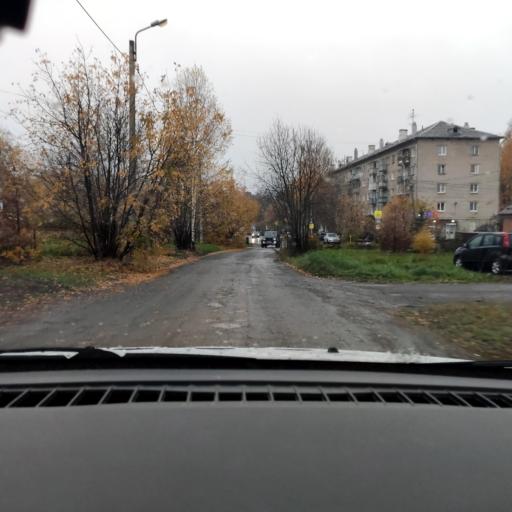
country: RU
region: Perm
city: Kondratovo
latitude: 58.0490
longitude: 56.0956
